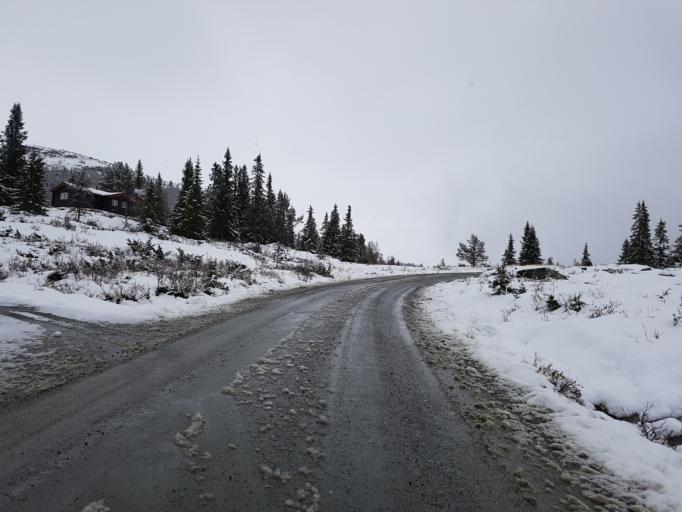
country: NO
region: Oppland
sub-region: Sel
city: Otta
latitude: 61.8057
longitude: 9.6906
